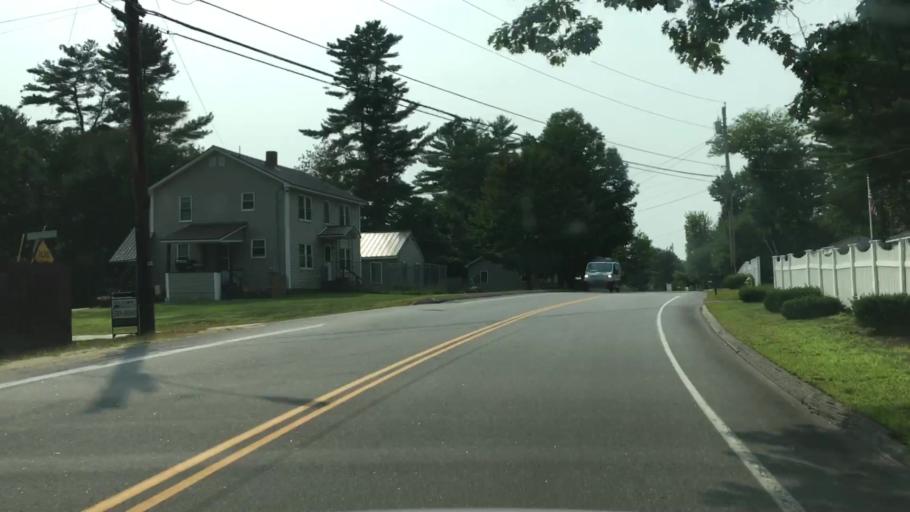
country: US
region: Maine
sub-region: Oxford County
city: South Paris
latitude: 44.2238
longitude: -70.4997
